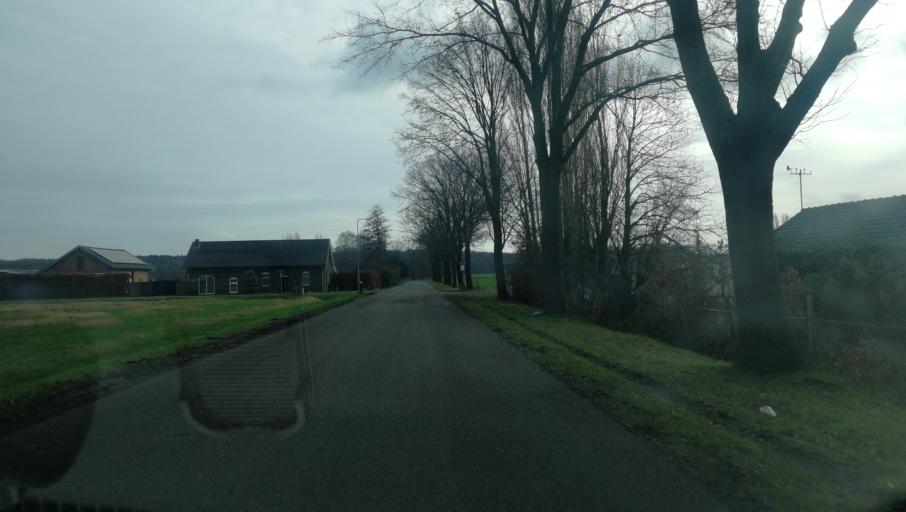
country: NL
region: Limburg
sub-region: Gemeente Beesel
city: Offenbeek
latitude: 51.3011
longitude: 6.1280
